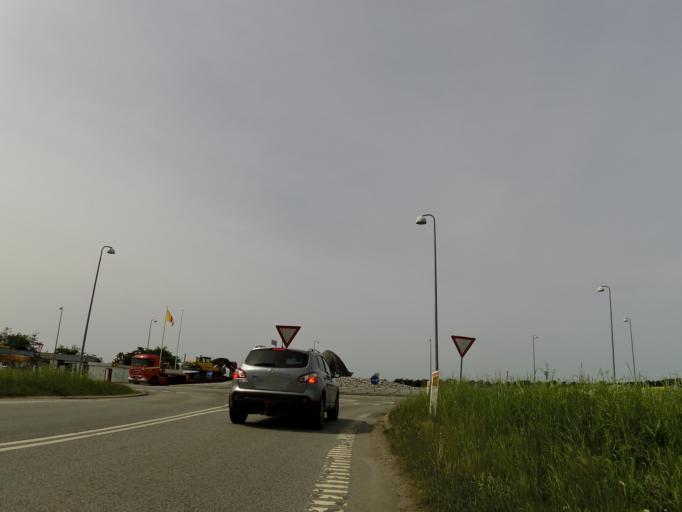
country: DK
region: Central Jutland
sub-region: Holstebro Kommune
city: Vinderup
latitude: 56.5696
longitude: 8.8709
